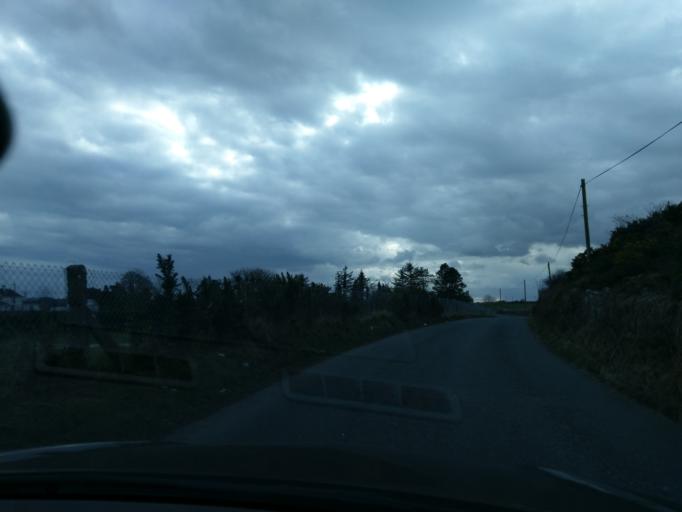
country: IE
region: Connaught
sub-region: County Galway
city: Athenry
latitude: 53.4675
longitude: -8.6641
